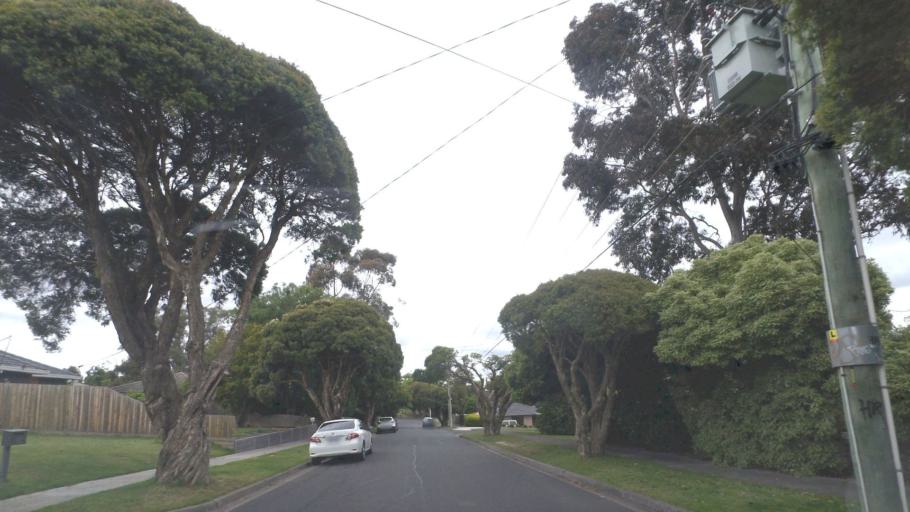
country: AU
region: Victoria
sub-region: Maroondah
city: Croydon South
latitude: -37.8133
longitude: 145.2824
